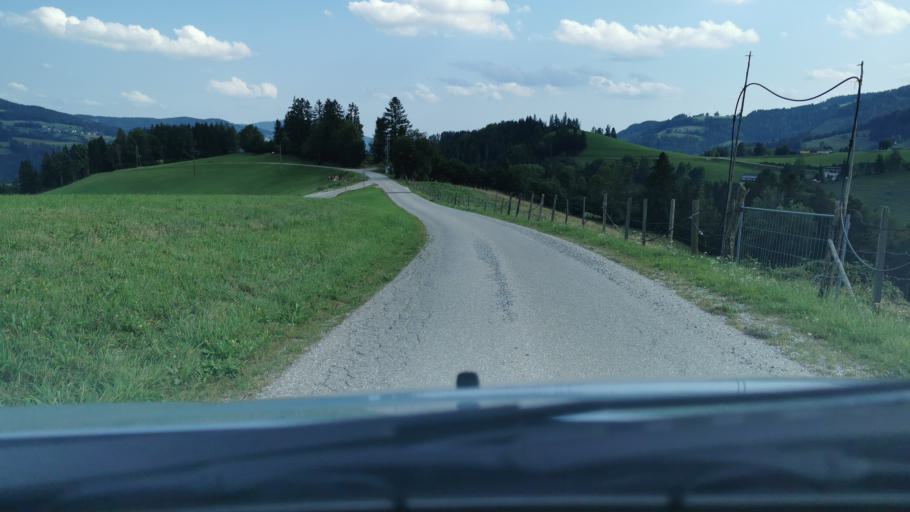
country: AT
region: Styria
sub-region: Politischer Bezirk Weiz
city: Koglhof
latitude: 47.3153
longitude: 15.6727
